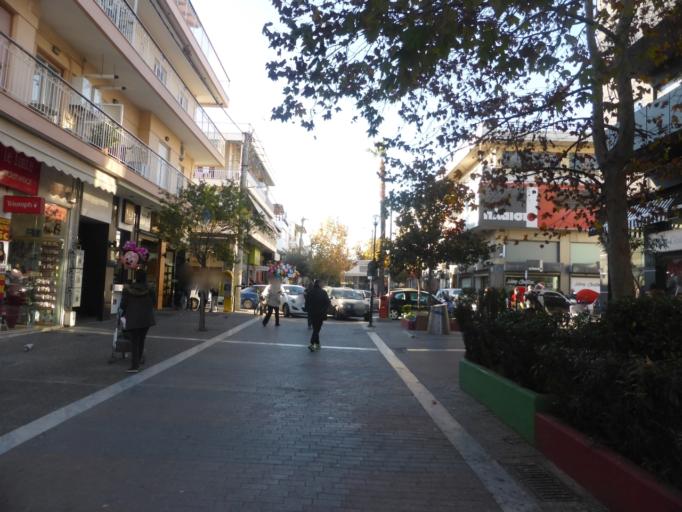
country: GR
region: Attica
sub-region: Nomarchia Athinas
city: Peristeri
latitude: 38.0127
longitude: 23.6918
